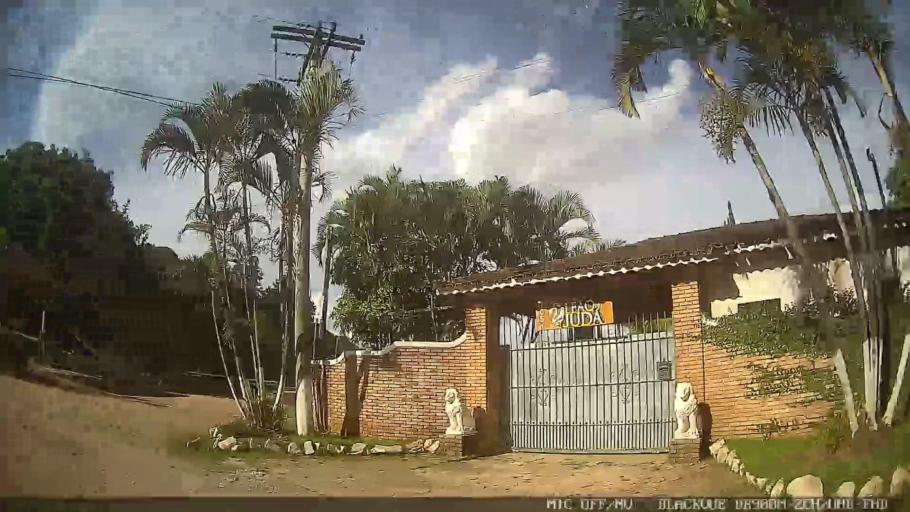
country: BR
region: Sao Paulo
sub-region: Bom Jesus Dos Perdoes
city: Bom Jesus dos Perdoes
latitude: -23.1222
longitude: -46.4958
